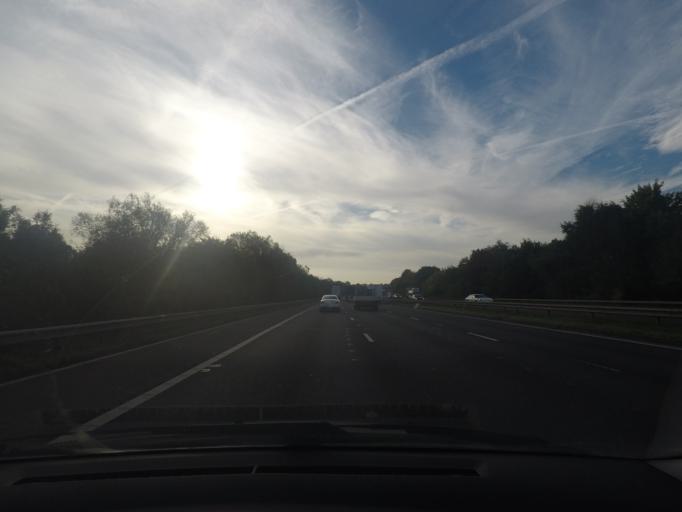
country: GB
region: England
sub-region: Barnsley
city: Darton
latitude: 53.5906
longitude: -1.5375
